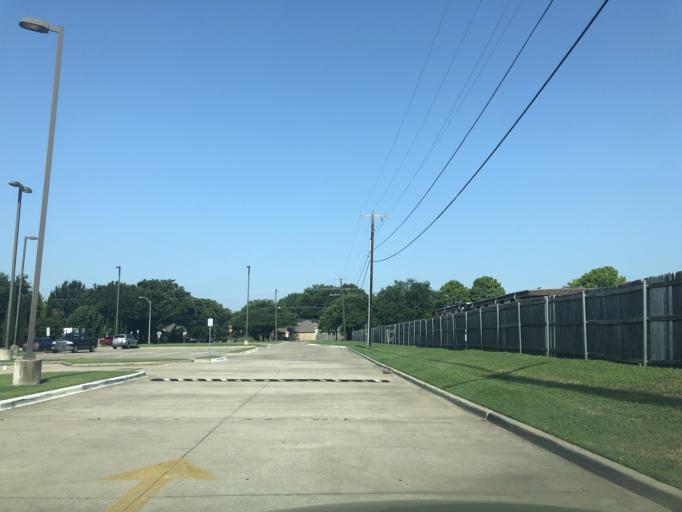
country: US
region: Texas
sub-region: Dallas County
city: Irving
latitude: 32.8071
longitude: -96.9751
